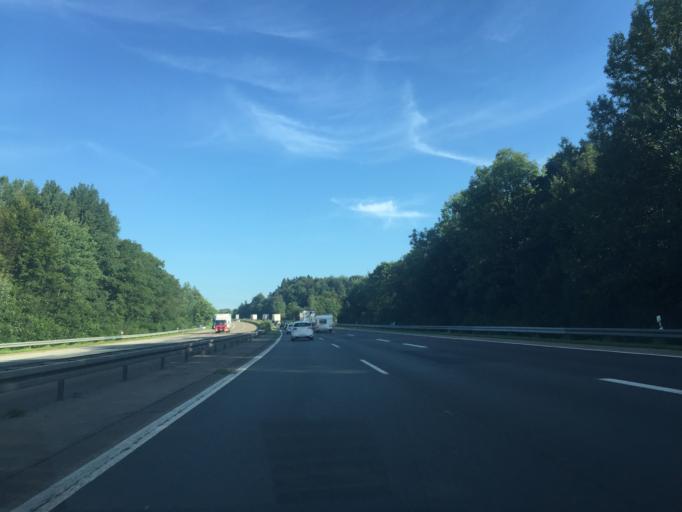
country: DE
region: North Rhine-Westphalia
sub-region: Regierungsbezirk Arnsberg
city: Olpe
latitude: 51.0313
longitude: 7.8233
